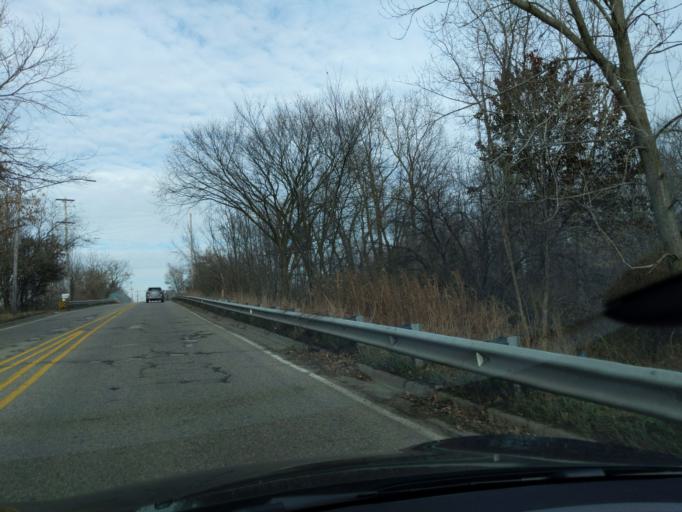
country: US
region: Michigan
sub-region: Ingham County
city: Holt
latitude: 42.6628
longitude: -84.5235
